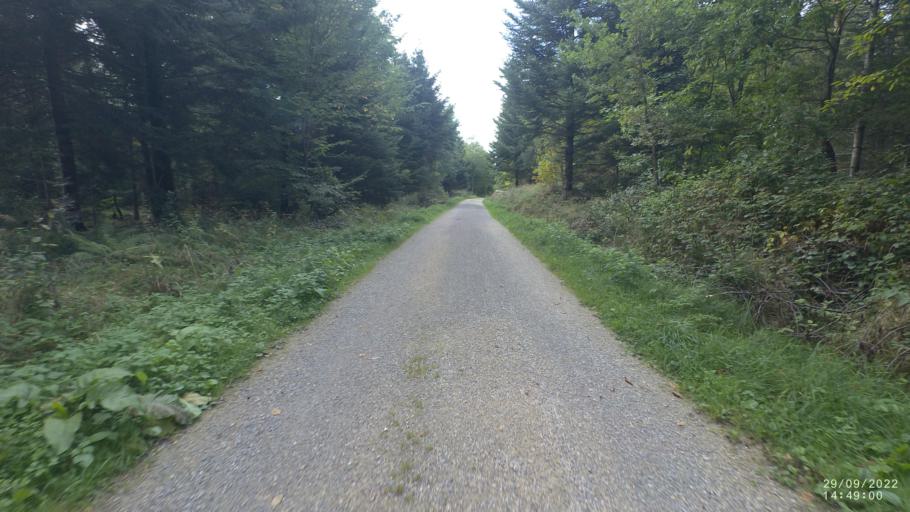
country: DE
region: Baden-Wuerttemberg
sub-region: Regierungsbezirk Stuttgart
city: Adelberg
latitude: 48.7747
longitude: 9.5836
